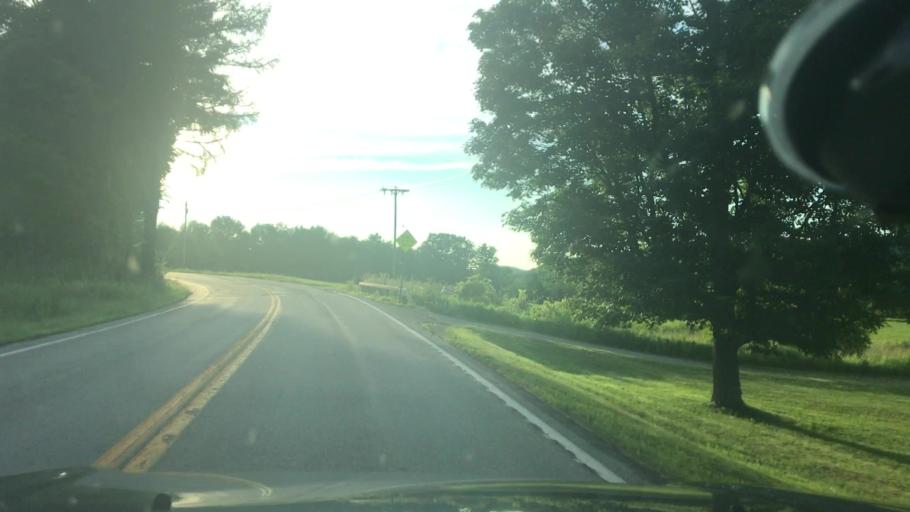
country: US
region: New York
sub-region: Otsego County
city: Unadilla
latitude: 42.3378
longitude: -75.2431
